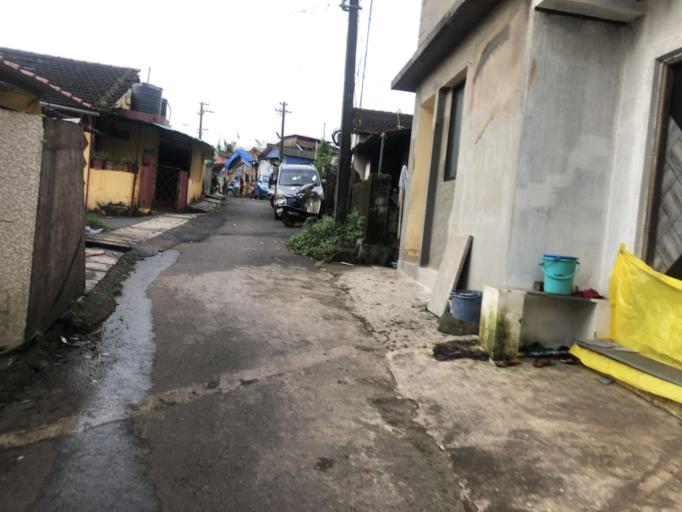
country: IN
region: Goa
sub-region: North Goa
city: Serula
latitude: 15.5487
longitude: 73.8254
